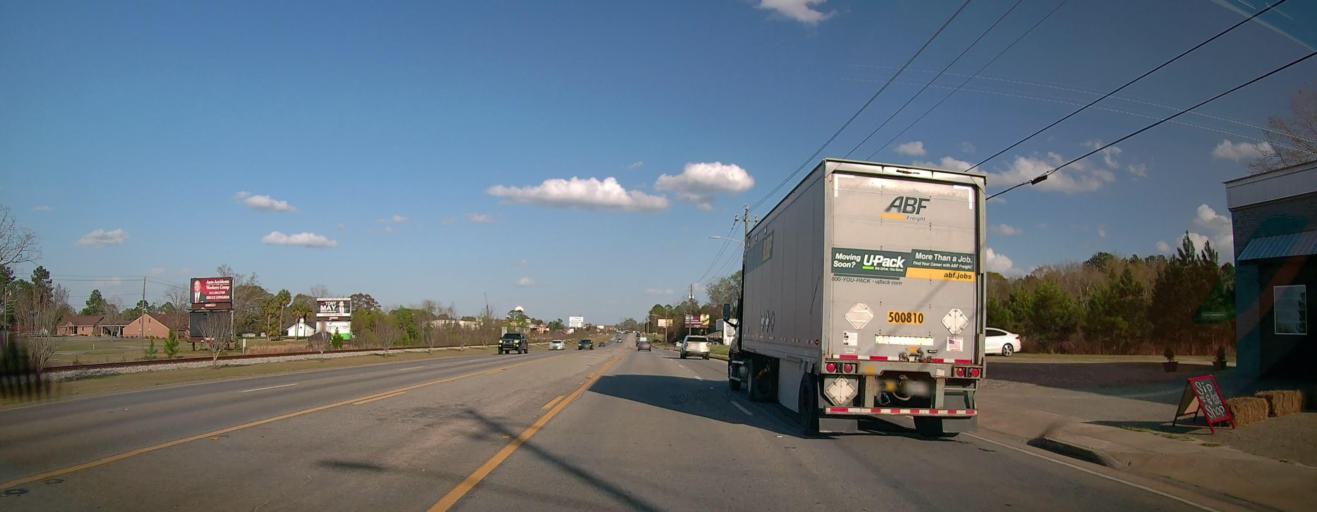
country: US
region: Georgia
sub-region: Toombs County
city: Lyons
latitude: 32.2018
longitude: -82.3368
